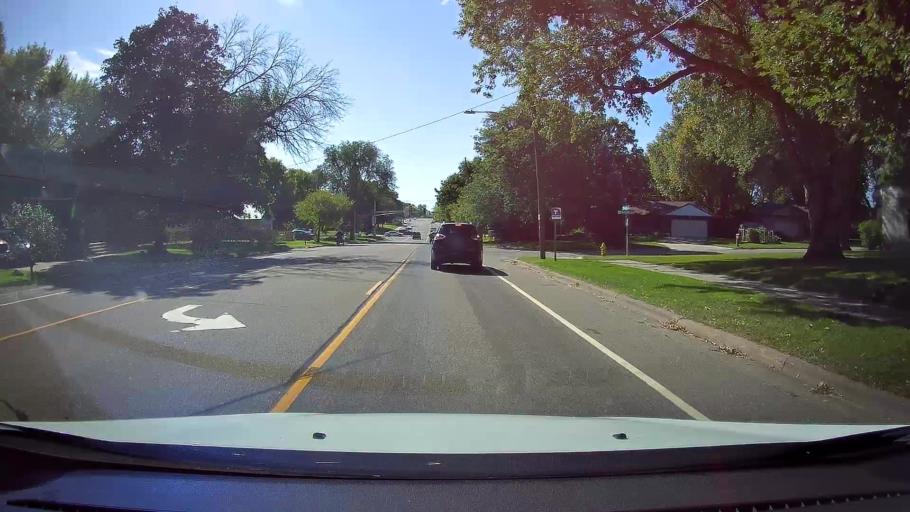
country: US
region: Minnesota
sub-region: Ramsey County
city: Roseville
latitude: 45.0147
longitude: -93.1568
